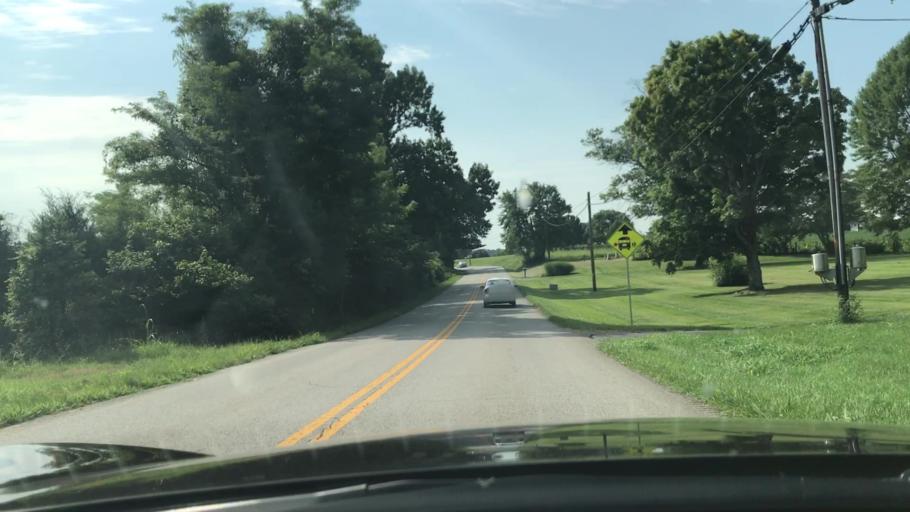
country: US
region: Kentucky
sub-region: Green County
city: Greensburg
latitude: 37.2637
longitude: -85.5601
